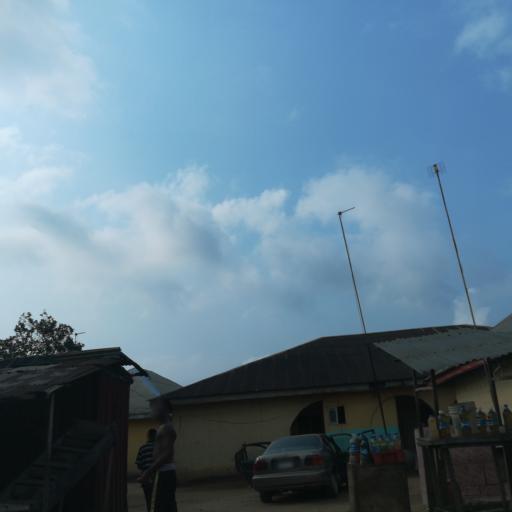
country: NG
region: Rivers
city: Okrika
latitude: 4.7835
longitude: 7.1401
